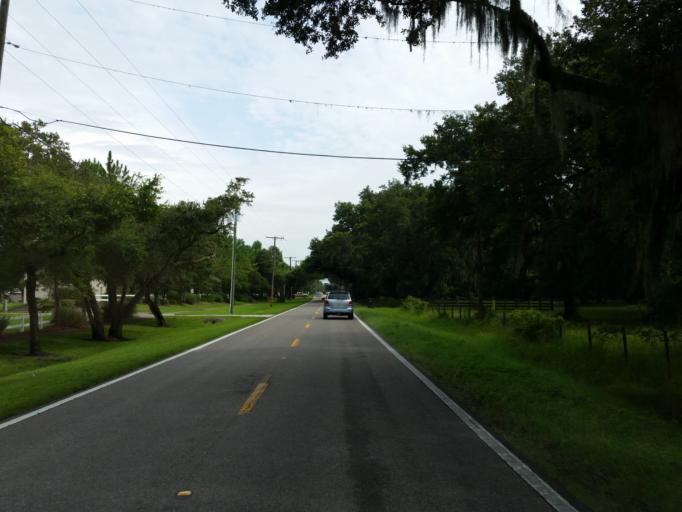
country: US
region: Florida
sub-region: Hillsborough County
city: Seffner
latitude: 27.9842
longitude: -82.2530
